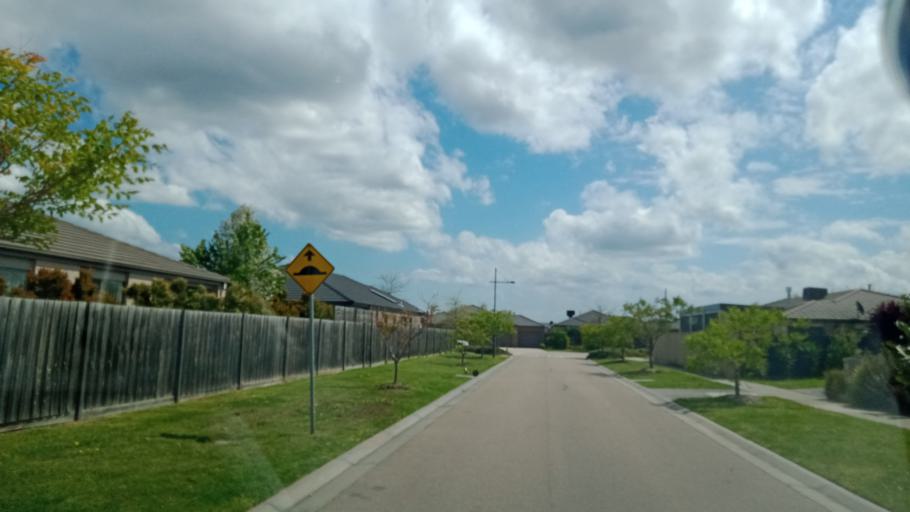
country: AU
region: Victoria
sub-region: Frankston
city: Sandhurst
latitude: -38.0833
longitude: 145.2002
